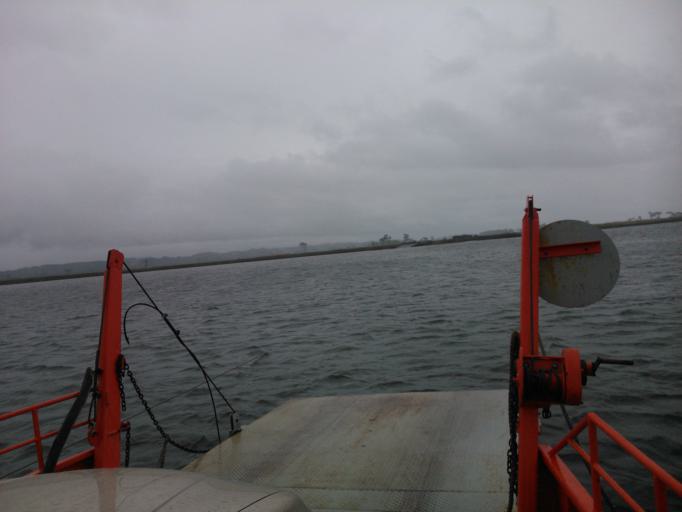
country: CL
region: Araucania
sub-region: Provincia de Cautin
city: Carahue
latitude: -38.7472
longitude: -73.4083
